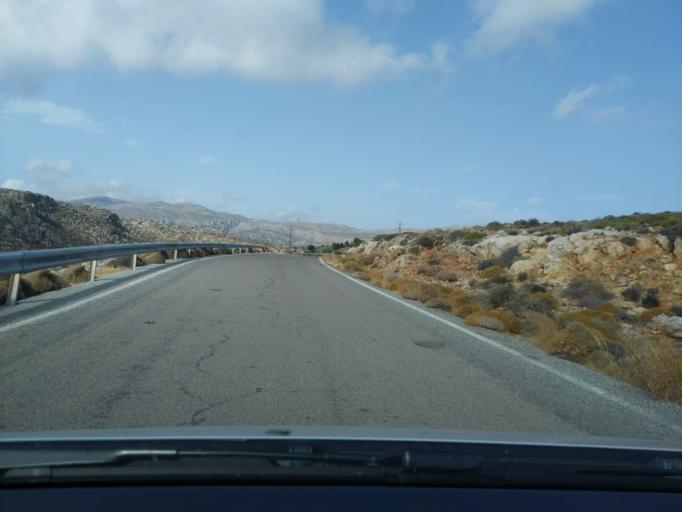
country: GR
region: Crete
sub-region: Nomos Lasithiou
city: Palekastro
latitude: 35.0848
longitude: 26.2577
